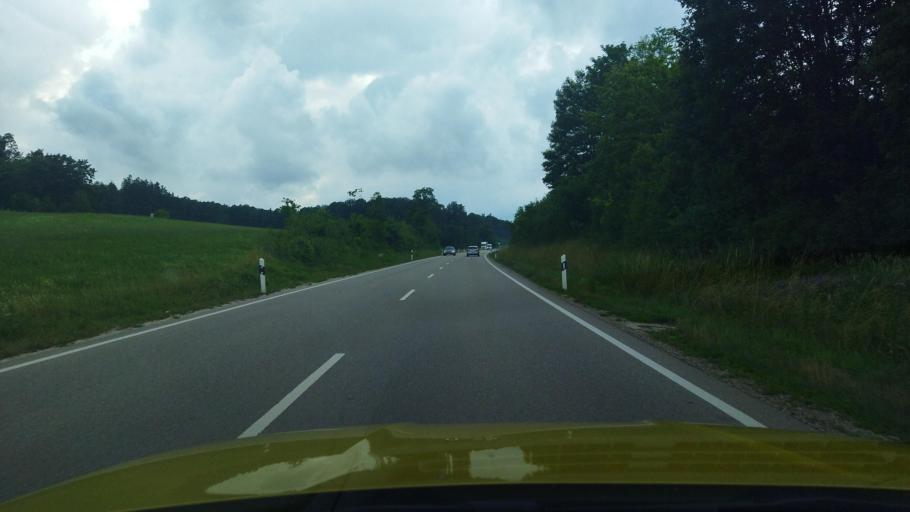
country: DE
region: Bavaria
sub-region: Regierungsbezirk Mittelfranken
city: Pfofeld
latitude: 49.1149
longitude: 10.8543
